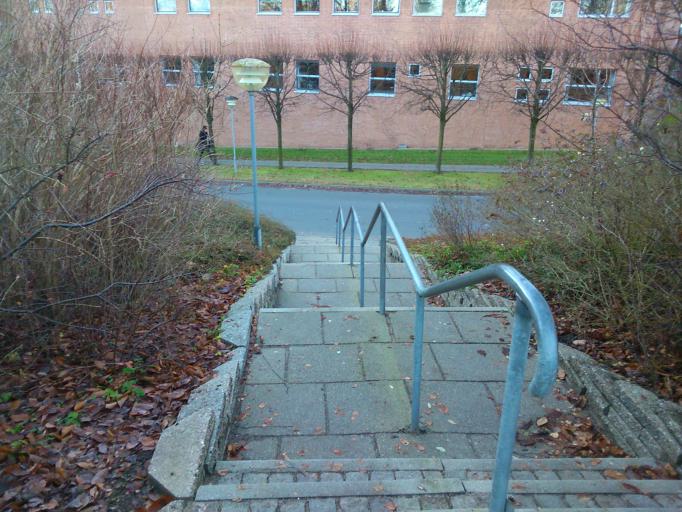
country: DK
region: Central Jutland
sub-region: Holstebro Kommune
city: Holstebro
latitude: 56.3621
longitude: 8.6245
